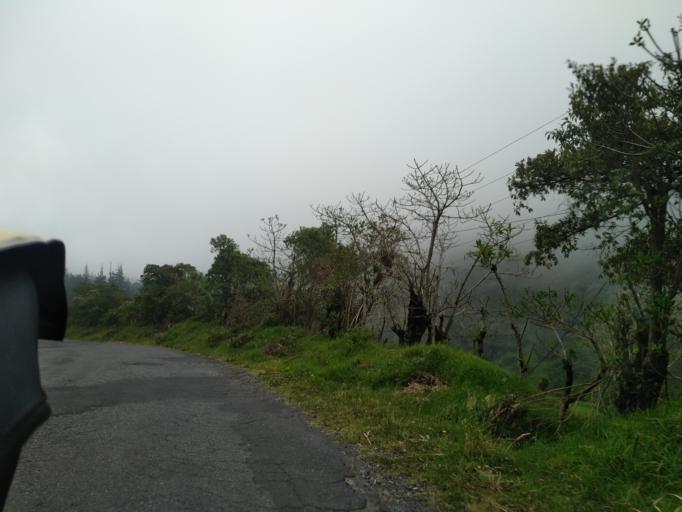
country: EC
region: Cotopaxi
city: Saquisili
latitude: -0.6938
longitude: -78.8168
